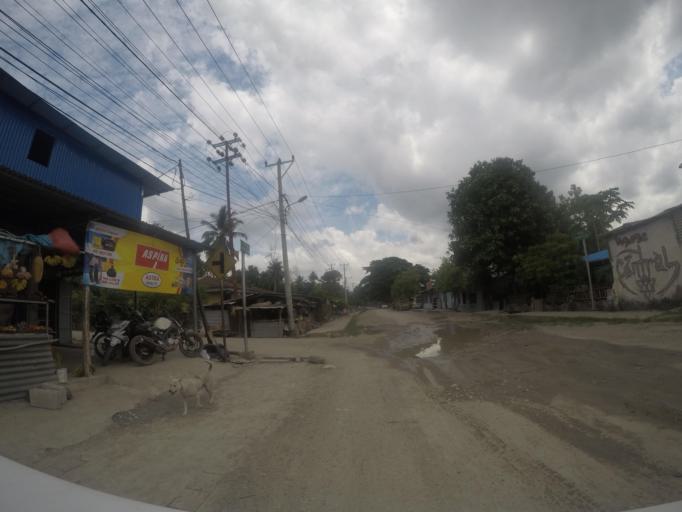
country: TL
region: Viqueque
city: Viqueque
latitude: -8.8586
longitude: 126.3652
